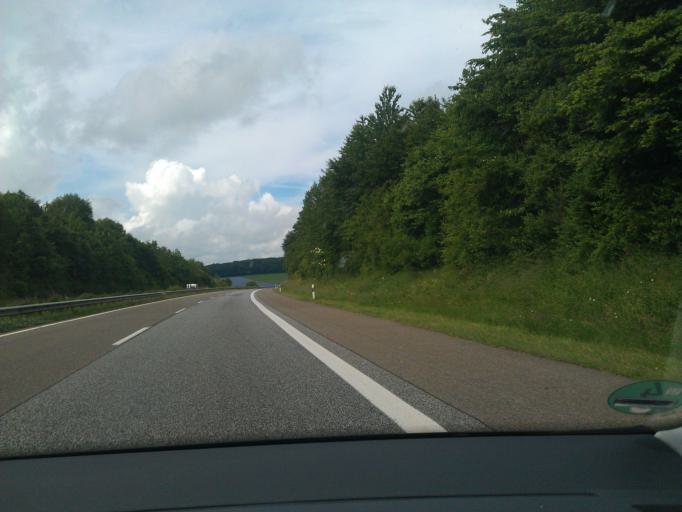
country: DE
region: Rheinland-Pfalz
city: Winringen
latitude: 50.1418
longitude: 6.4056
